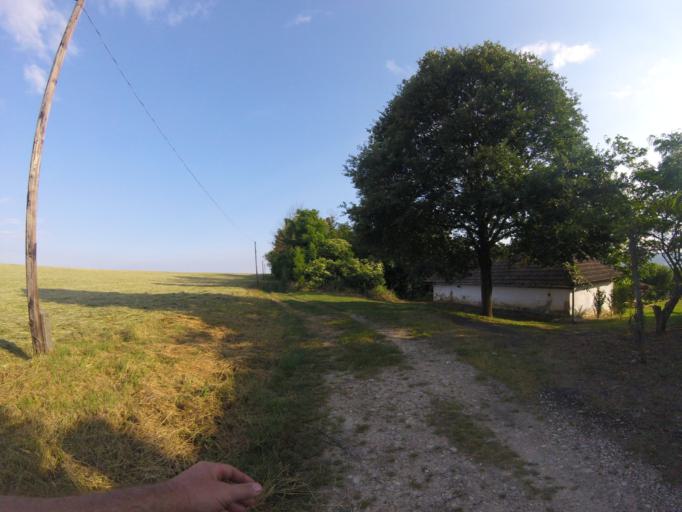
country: HU
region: Zala
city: Zalaszentgrot
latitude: 46.8872
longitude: 17.1308
